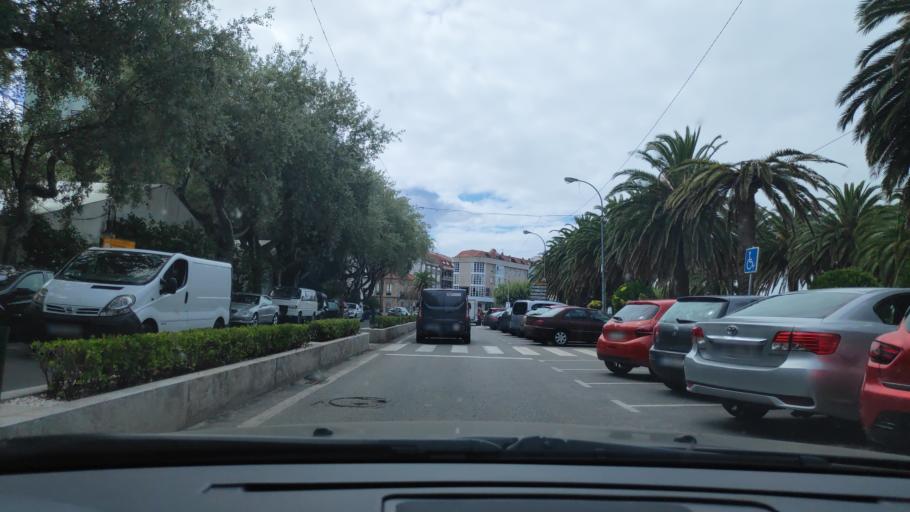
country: ES
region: Galicia
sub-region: Provincia de Pontevedra
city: Cambados
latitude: 42.5164
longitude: -8.8150
